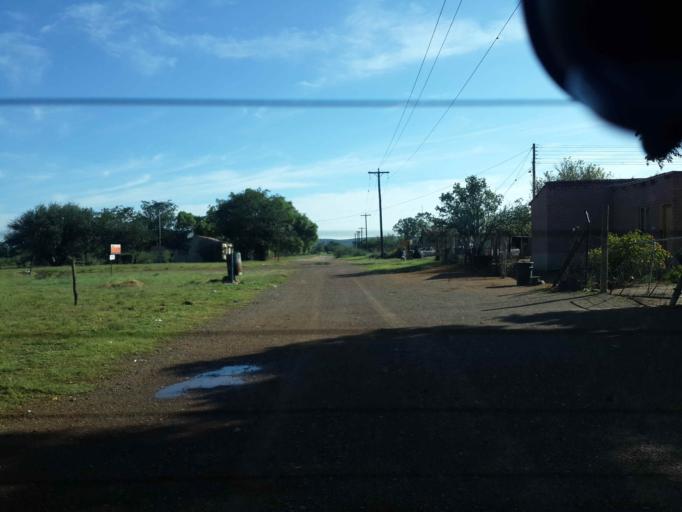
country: ZA
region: Northern Cape
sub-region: Siyanda District Municipality
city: Danielskuil
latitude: -28.1951
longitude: 23.5298
